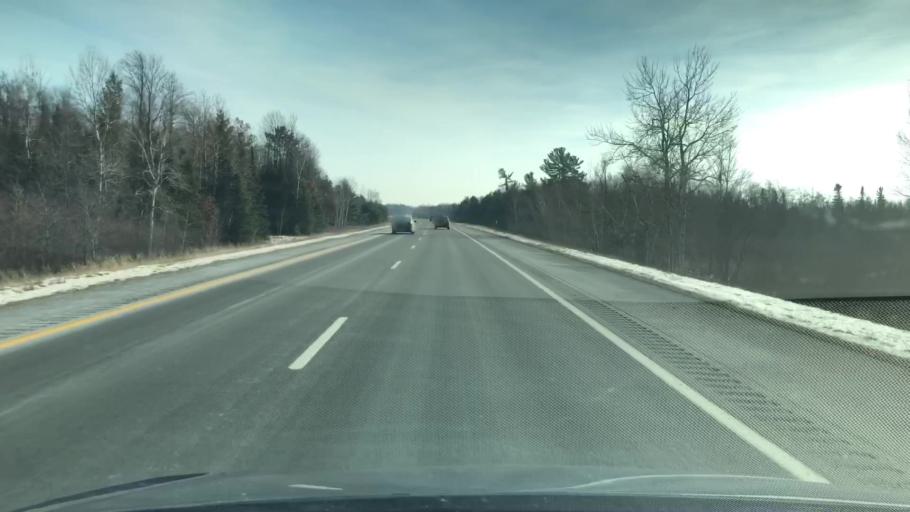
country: US
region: Michigan
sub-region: Roscommon County
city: Prudenville
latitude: 44.3403
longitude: -84.5541
